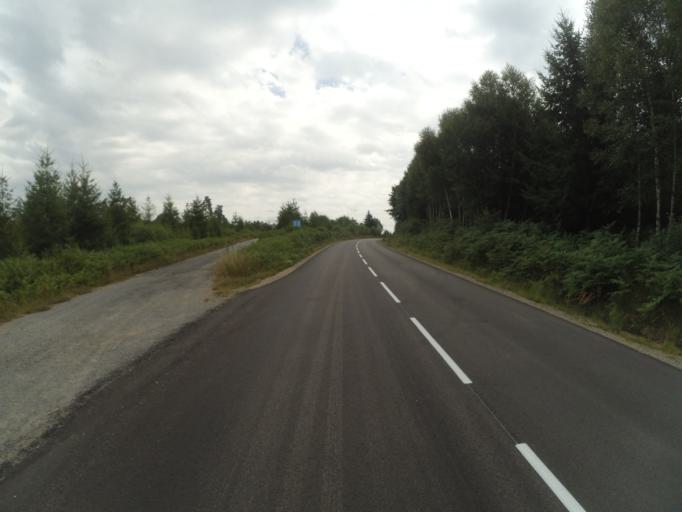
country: FR
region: Limousin
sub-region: Departement de la Creuse
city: La Courtine
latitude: 45.6613
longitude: 2.2092
